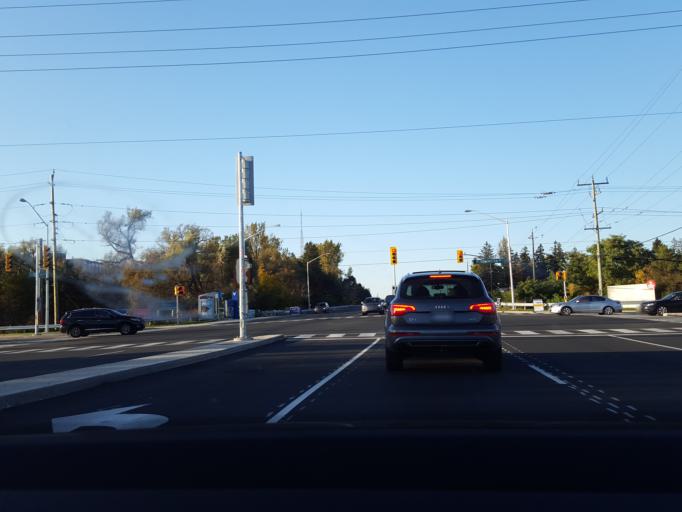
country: CA
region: Ontario
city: Newmarket
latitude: 43.9625
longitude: -79.4587
